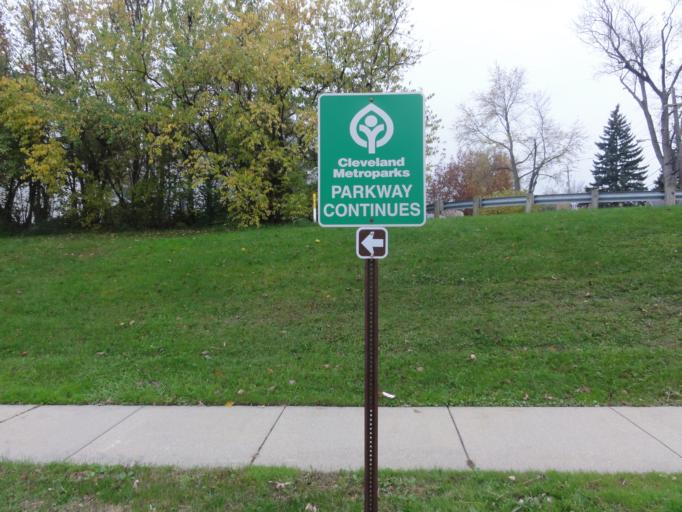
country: US
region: Ohio
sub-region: Cuyahoga County
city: Berea
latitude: 41.3768
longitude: -81.8663
